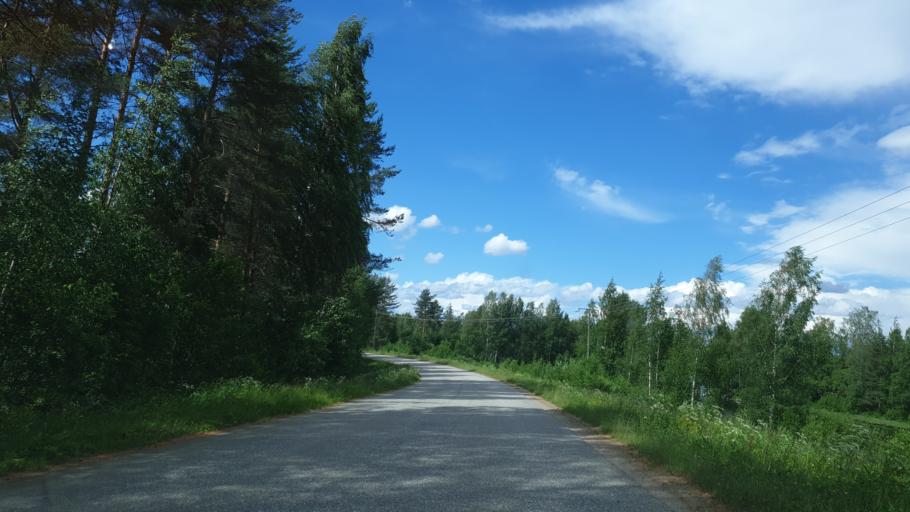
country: FI
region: Northern Savo
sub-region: Koillis-Savo
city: Kaavi
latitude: 62.9983
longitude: 28.7153
